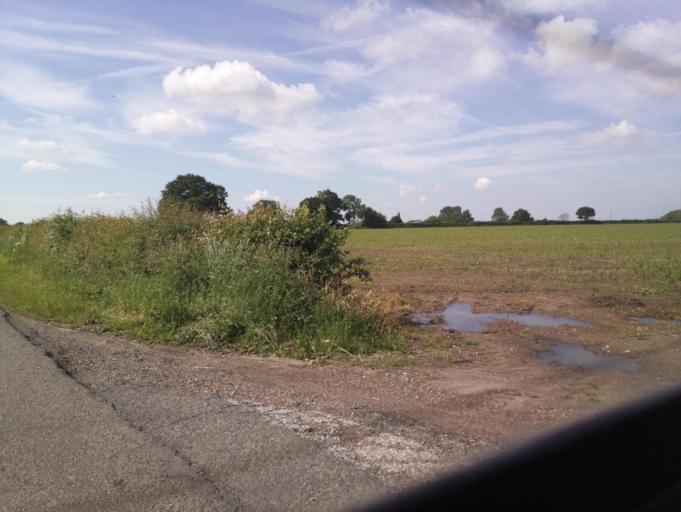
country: GB
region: England
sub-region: Lincolnshire
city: Skellingthorpe
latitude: 53.1397
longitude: -0.6332
